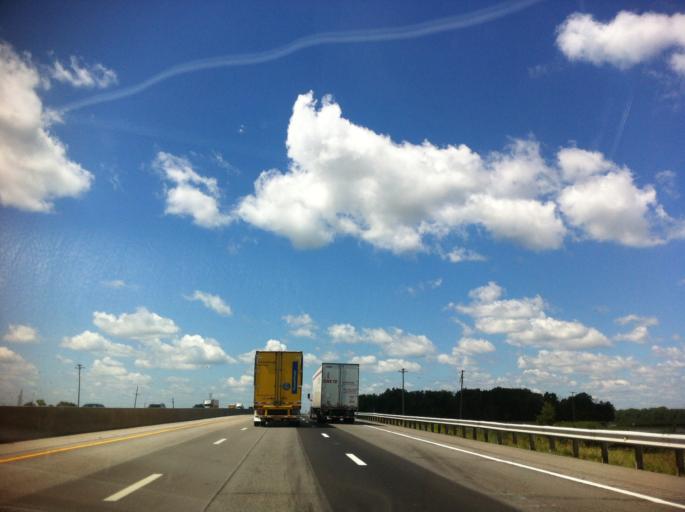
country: US
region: Ohio
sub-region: Wood County
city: Millbury
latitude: 41.5139
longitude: -83.4312
